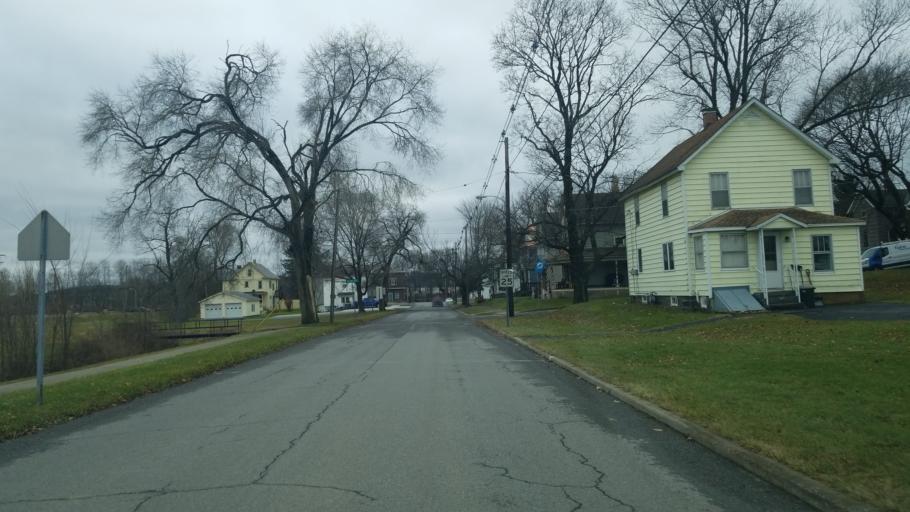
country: US
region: Pennsylvania
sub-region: Clearfield County
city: DuBois
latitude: 41.1300
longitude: -78.7596
